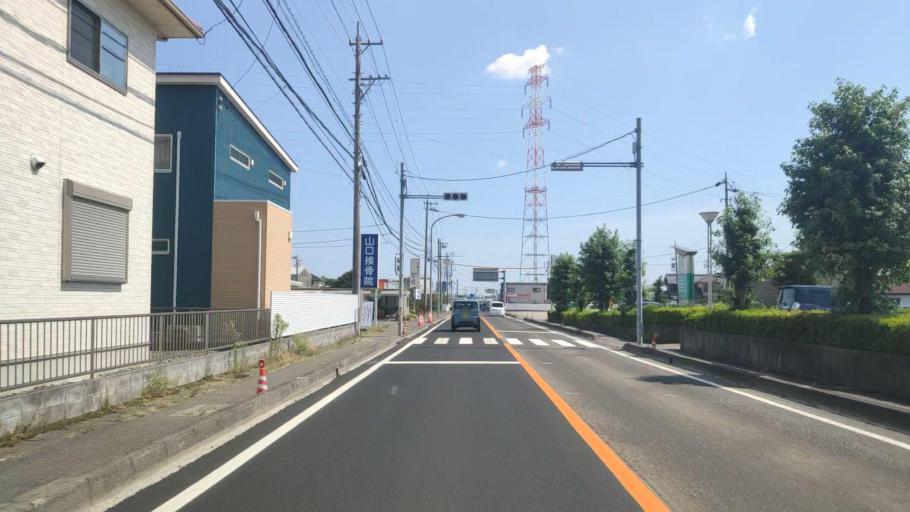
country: JP
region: Gifu
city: Godo
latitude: 35.4632
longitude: 136.6759
